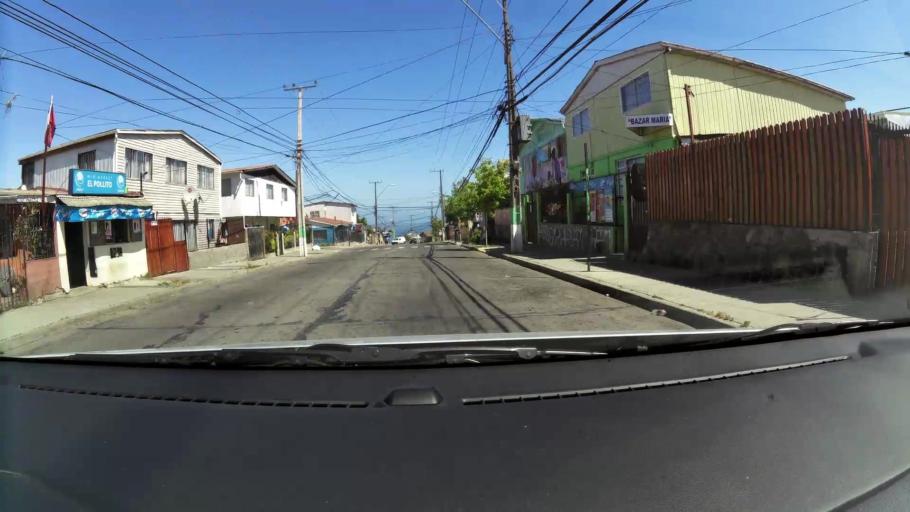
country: CL
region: Valparaiso
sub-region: Provincia de Valparaiso
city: Valparaiso
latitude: -33.0496
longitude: -71.5864
